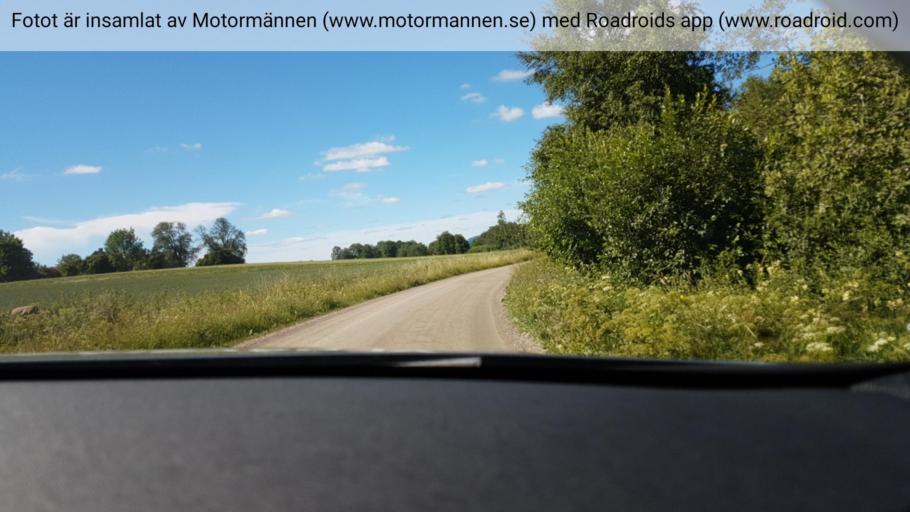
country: SE
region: Vaestra Goetaland
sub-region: Falkopings Kommun
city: Akarp
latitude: 58.2001
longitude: 13.7331
